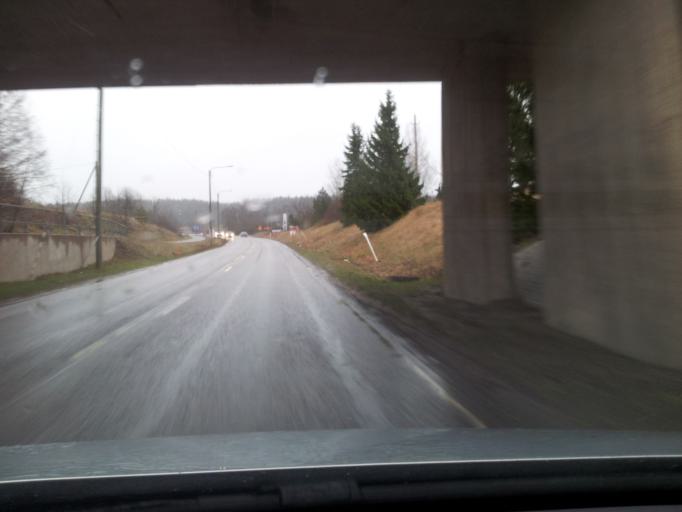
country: FI
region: Uusimaa
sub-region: Helsinki
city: Kirkkonummi
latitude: 60.1541
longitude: 24.5345
